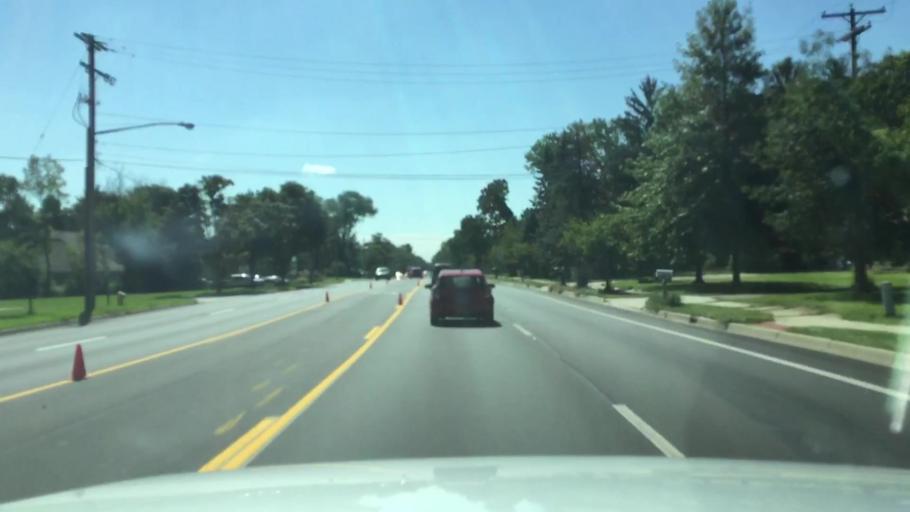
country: US
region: Michigan
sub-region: Kalamazoo County
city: Portage
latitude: 42.2350
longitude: -85.6141
